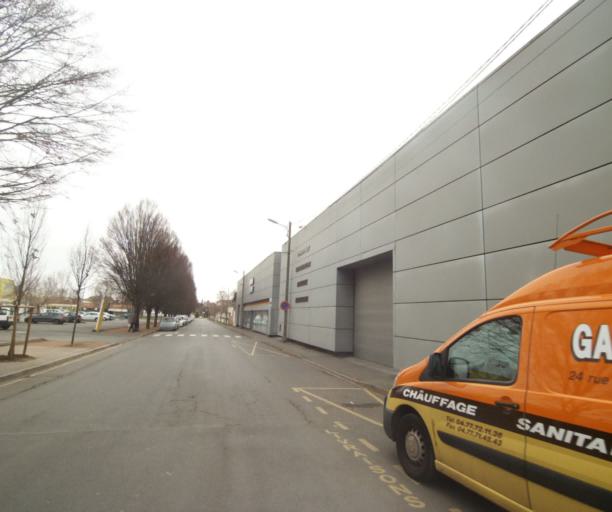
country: FR
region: Rhone-Alpes
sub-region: Departement de la Loire
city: Roanne
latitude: 46.0346
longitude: 4.0634
